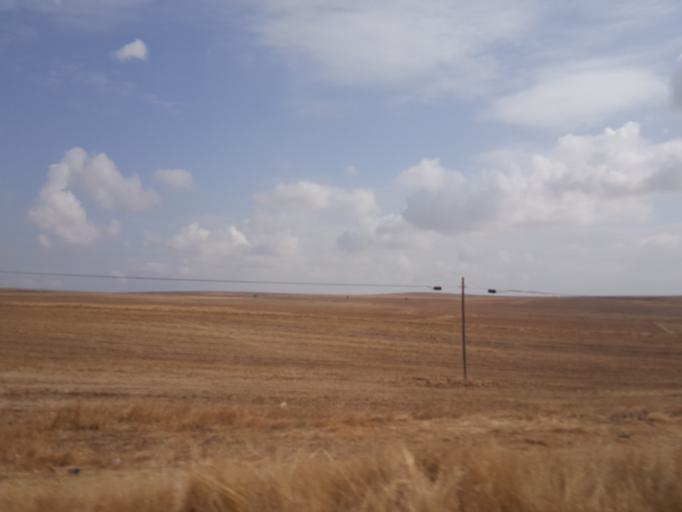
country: TR
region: Kirikkale
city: Keskin
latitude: 39.6134
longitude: 33.6130
